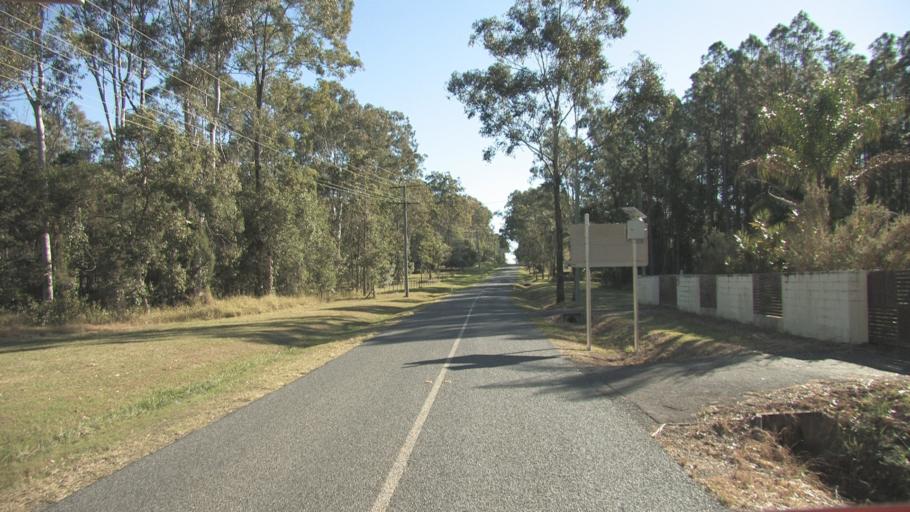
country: AU
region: Queensland
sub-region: Logan
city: Logan Reserve
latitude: -27.7403
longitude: 153.0991
